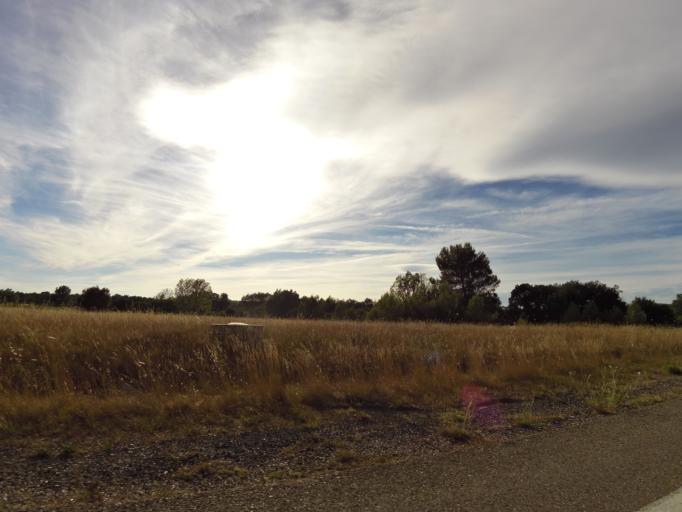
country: FR
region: Languedoc-Roussillon
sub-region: Departement du Gard
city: Saint-Mamert-du-Gard
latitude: 43.8409
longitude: 4.1415
